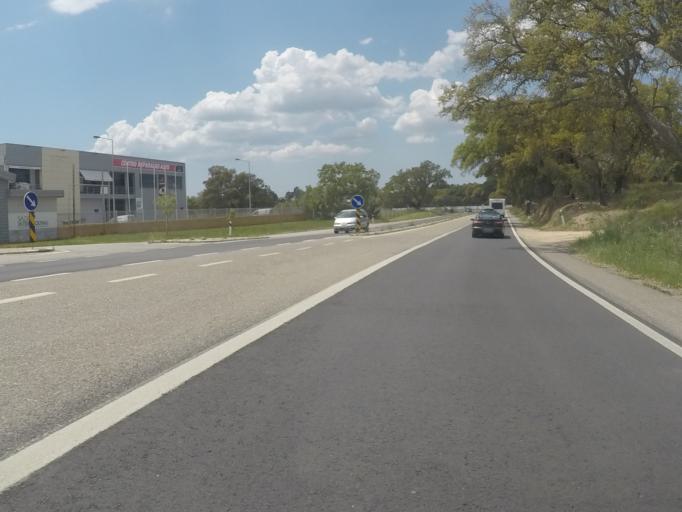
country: PT
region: Setubal
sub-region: Setubal
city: Setubal
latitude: 38.5441
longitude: -8.8264
